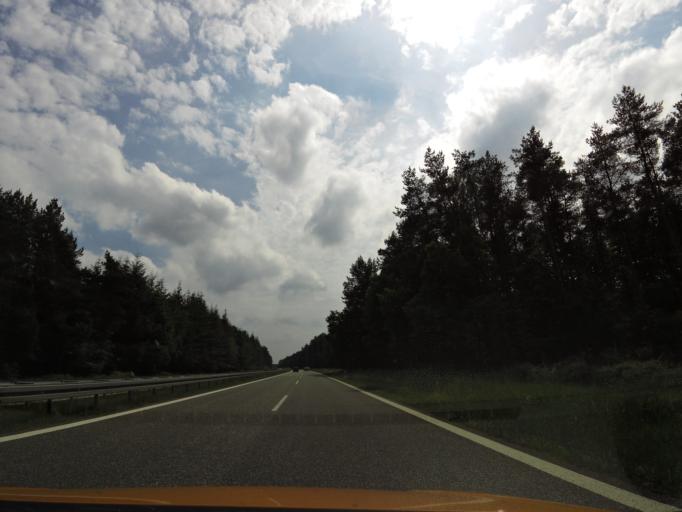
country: DE
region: Mecklenburg-Vorpommern
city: Mirow
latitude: 53.5185
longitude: 11.4672
